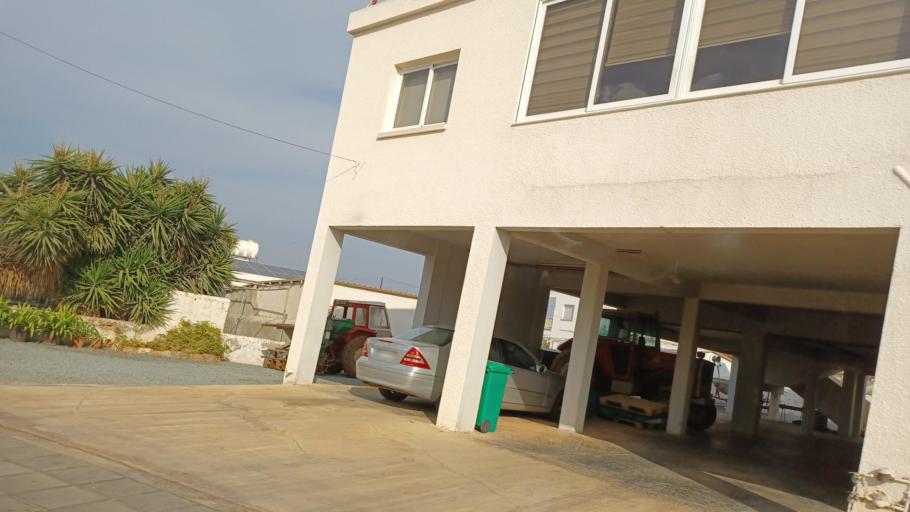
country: CY
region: Ammochostos
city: Frenaros
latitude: 35.0418
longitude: 33.9217
